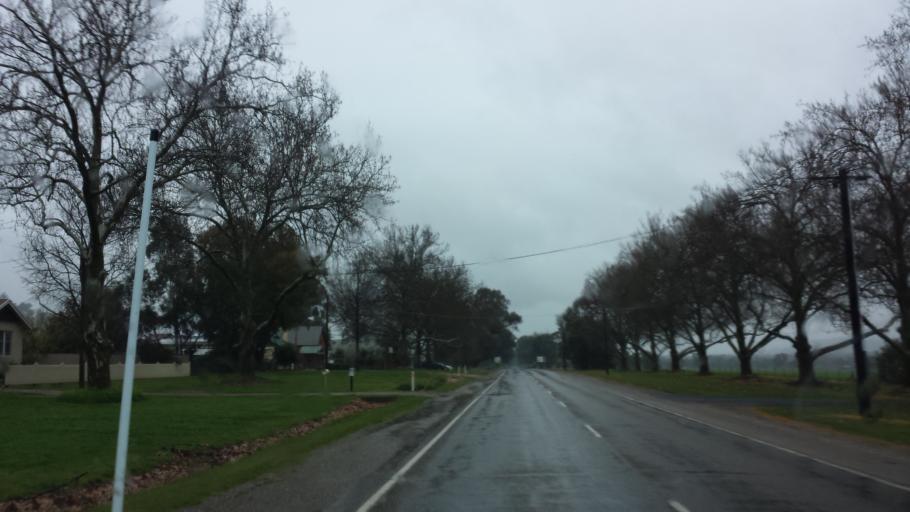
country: AU
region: Victoria
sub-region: Wangaratta
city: Wangaratta
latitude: -36.4347
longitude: 146.5438
